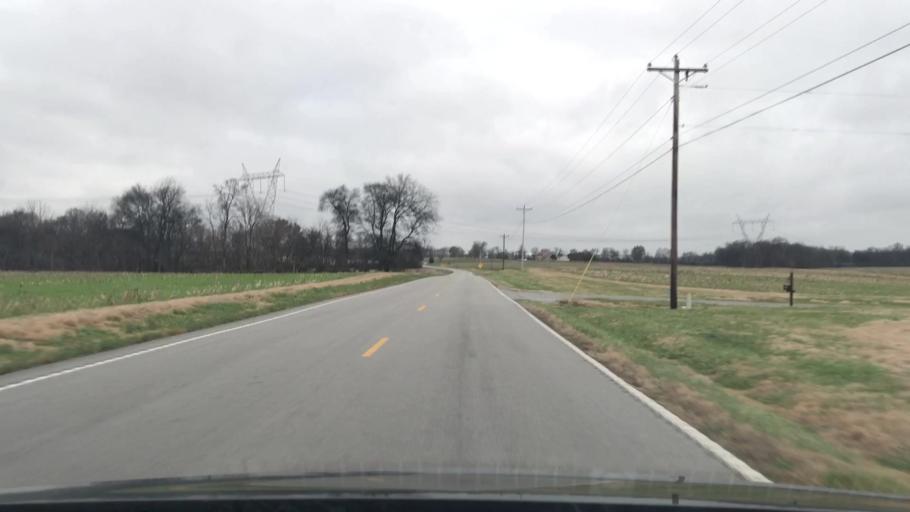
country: US
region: Kentucky
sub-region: Todd County
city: Guthrie
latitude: 36.6651
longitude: -87.1983
